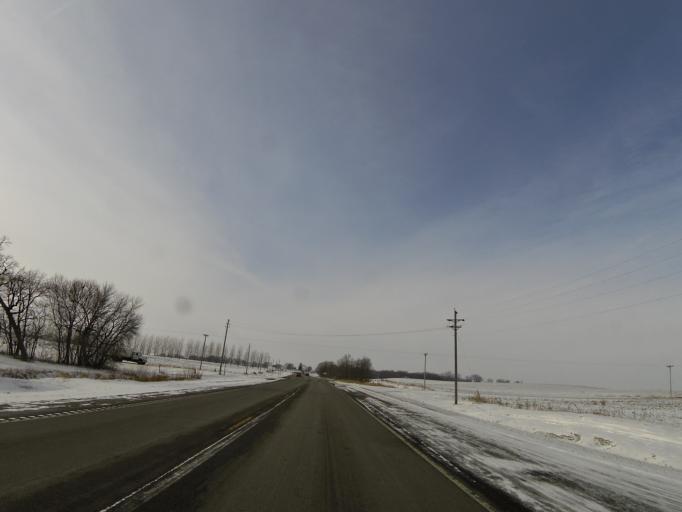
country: US
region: Minnesota
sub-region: McLeod County
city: Lester Prairie
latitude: 44.9063
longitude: -94.0722
